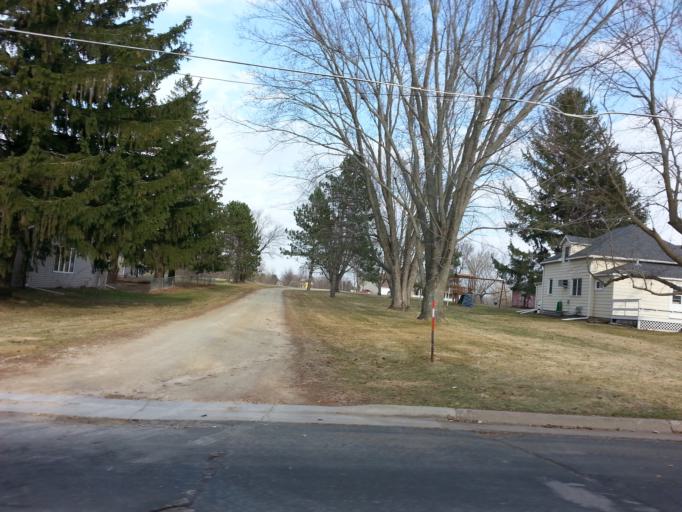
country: US
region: Wisconsin
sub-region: Pierce County
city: Ellsworth
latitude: 44.7202
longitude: -92.4799
